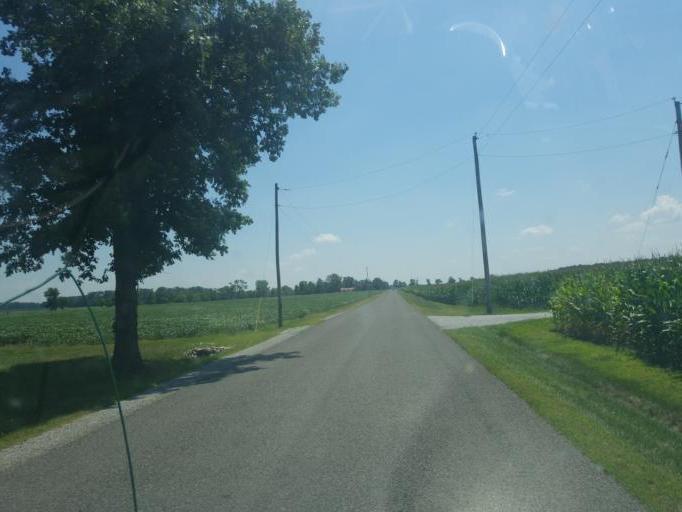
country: US
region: Ohio
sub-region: Auglaize County
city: Wapakoneta
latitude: 40.5372
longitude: -84.2310
